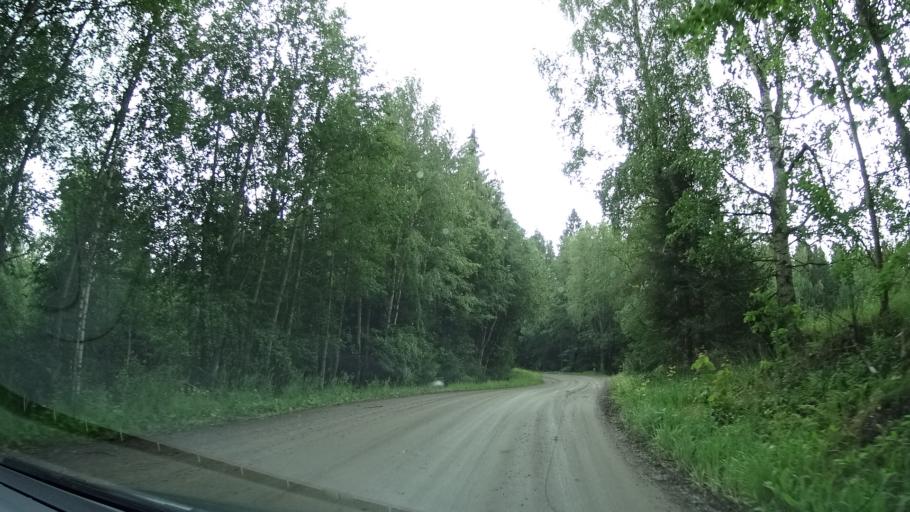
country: FI
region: Pirkanmaa
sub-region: Lounais-Pirkanmaa
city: Punkalaidun
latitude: 61.1056
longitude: 23.2748
